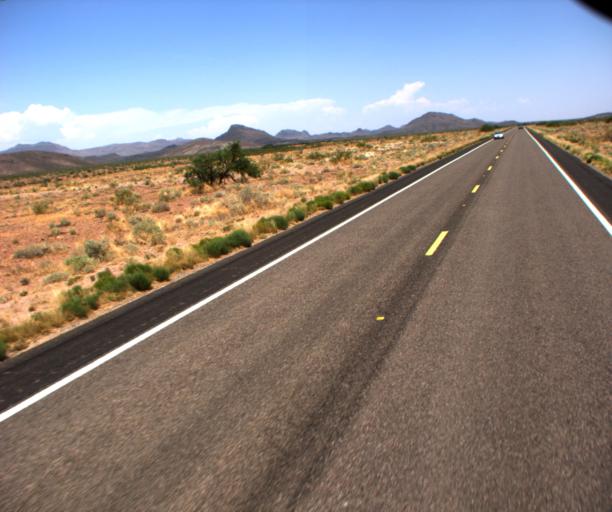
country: US
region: Arizona
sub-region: Graham County
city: Cactus Flat
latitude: 32.7663
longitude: -109.4608
